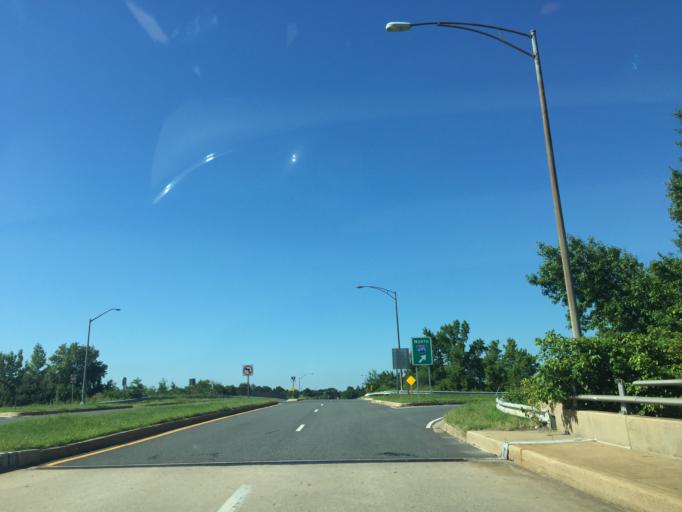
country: US
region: Maryland
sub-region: Baltimore County
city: Essex
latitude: 39.2791
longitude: -76.4718
